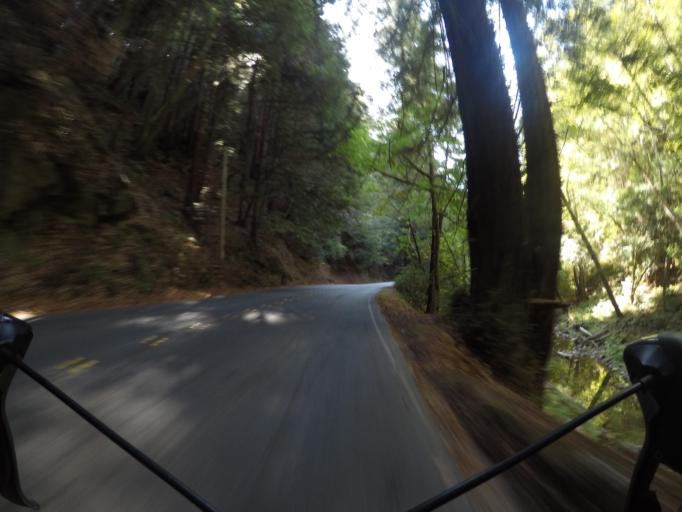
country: US
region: California
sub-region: San Mateo County
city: Portola Valley
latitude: 37.2664
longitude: -122.3137
